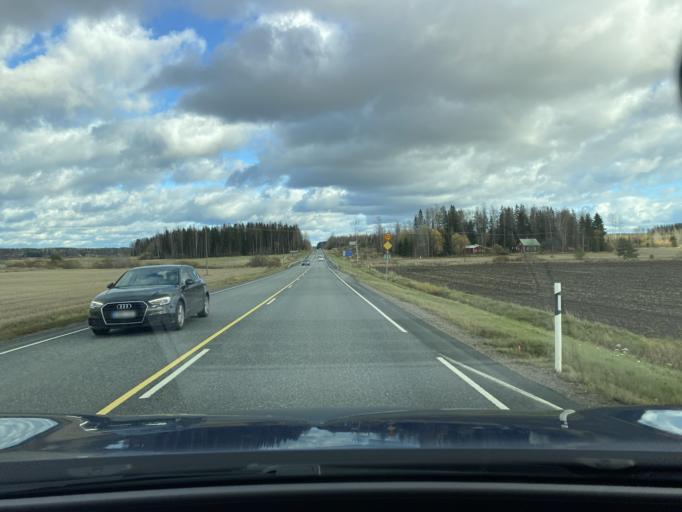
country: FI
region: Haeme
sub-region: Forssa
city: Humppila
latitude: 60.9413
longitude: 23.2859
